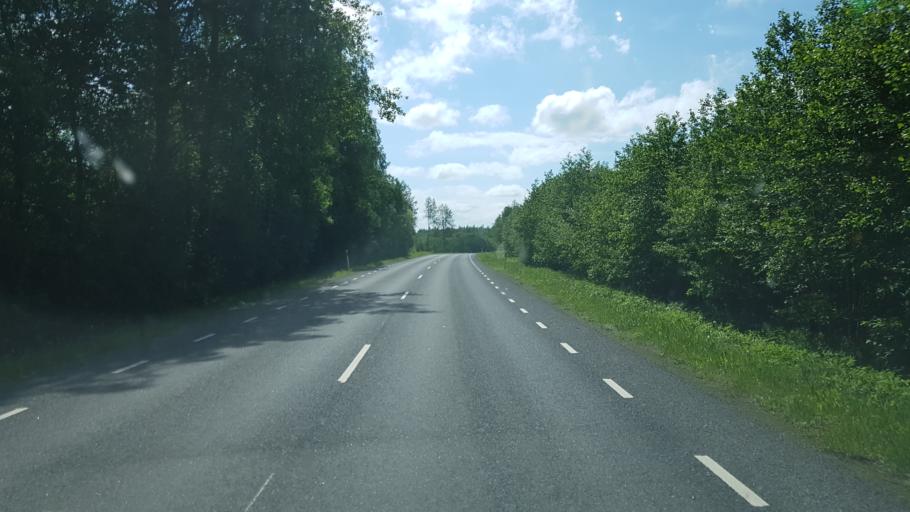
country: EE
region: Laeaene-Virumaa
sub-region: Rakke vald
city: Rakke
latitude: 58.9950
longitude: 26.2600
